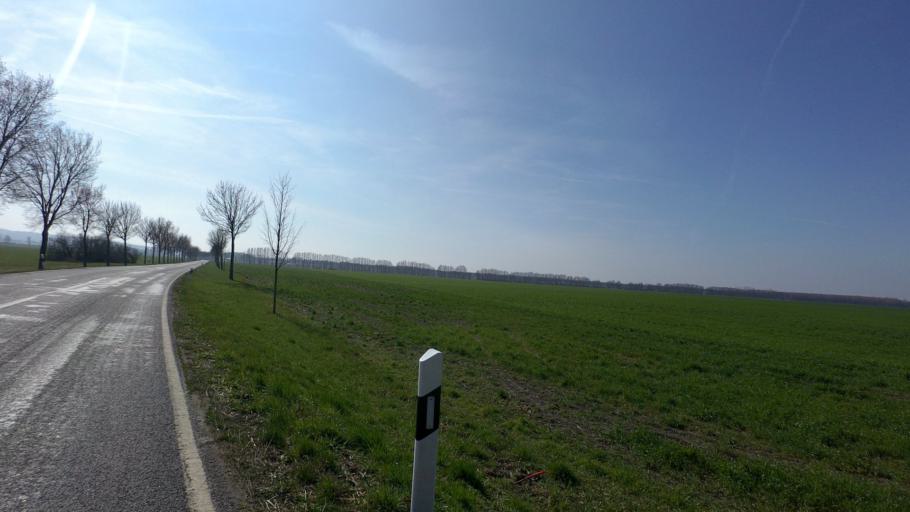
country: DE
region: Brandenburg
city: Sperenberg
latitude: 52.0666
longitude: 13.3251
